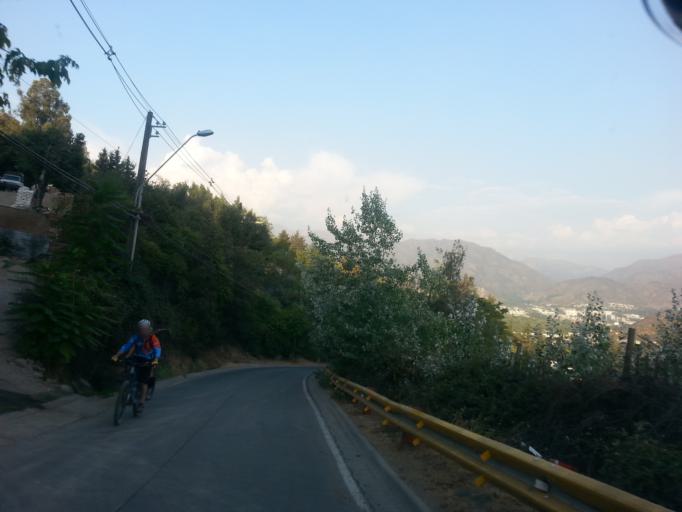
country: CL
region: Santiago Metropolitan
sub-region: Provincia de Santiago
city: Villa Presidente Frei, Nunoa, Santiago, Chile
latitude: -33.3636
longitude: -70.5563
